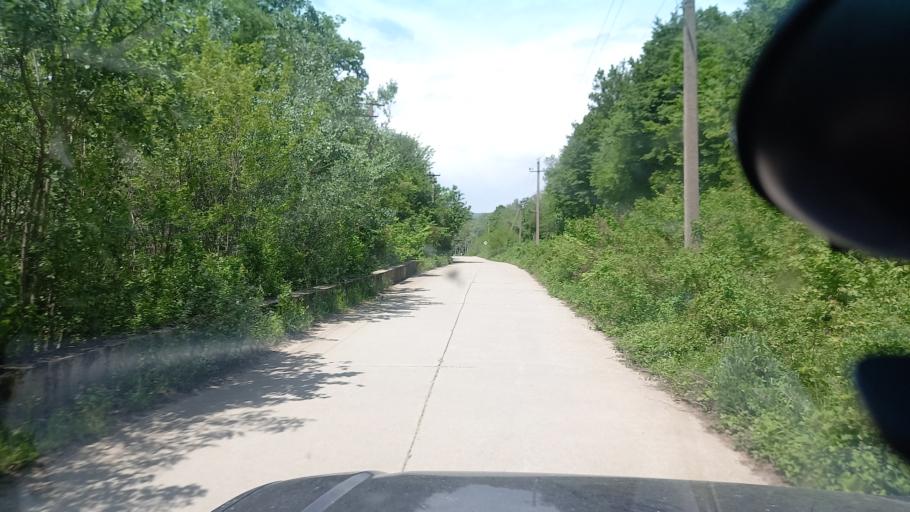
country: RU
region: Krasnodarskiy
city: Tuapse
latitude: 44.2457
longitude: 39.2396
